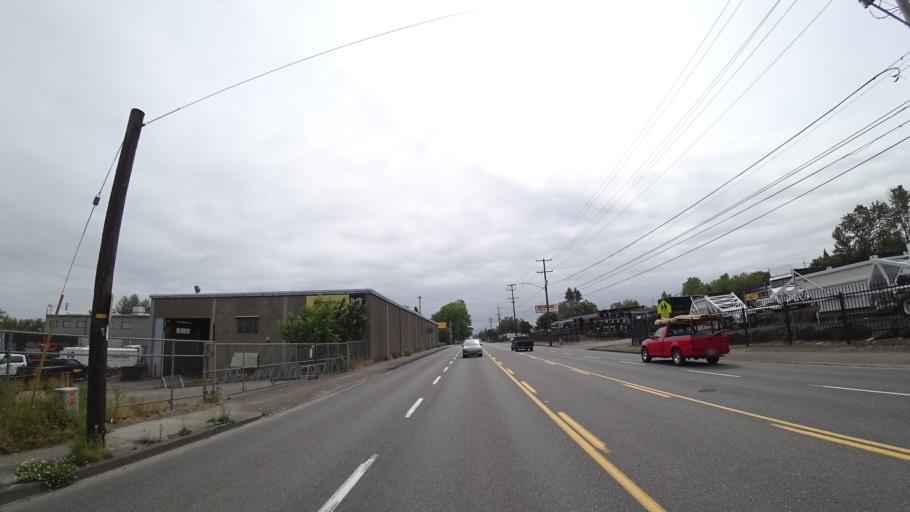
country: US
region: Oregon
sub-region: Multnomah County
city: Portland
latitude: 45.5705
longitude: -122.6127
